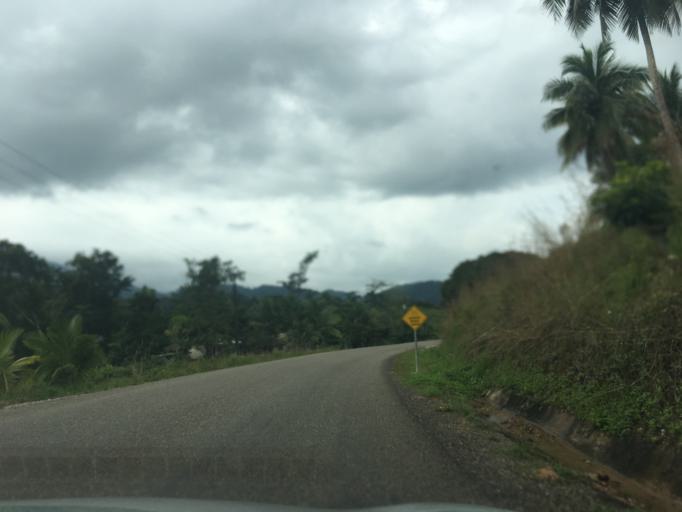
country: BZ
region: Cayo
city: Belmopan
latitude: 17.0901
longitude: -88.6530
